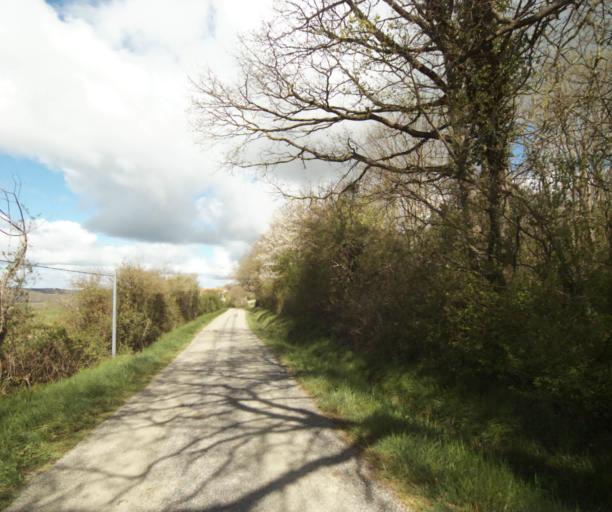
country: FR
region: Midi-Pyrenees
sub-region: Departement de l'Ariege
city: Saverdun
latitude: 43.1856
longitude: 1.5400
